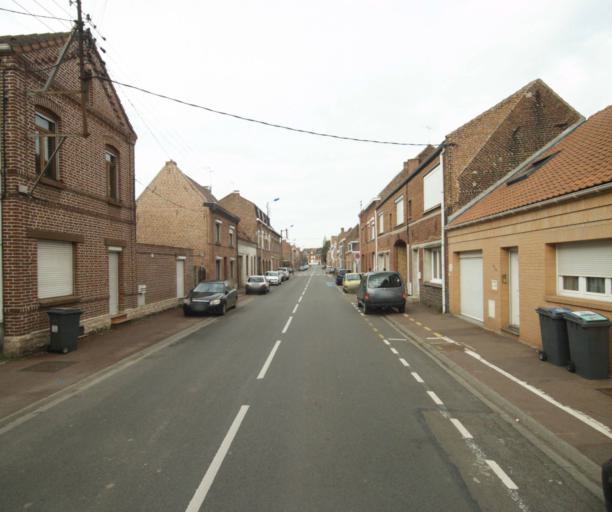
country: FR
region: Nord-Pas-de-Calais
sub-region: Departement du Nord
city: Sainghin-en-Weppes
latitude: 50.5585
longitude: 2.9066
